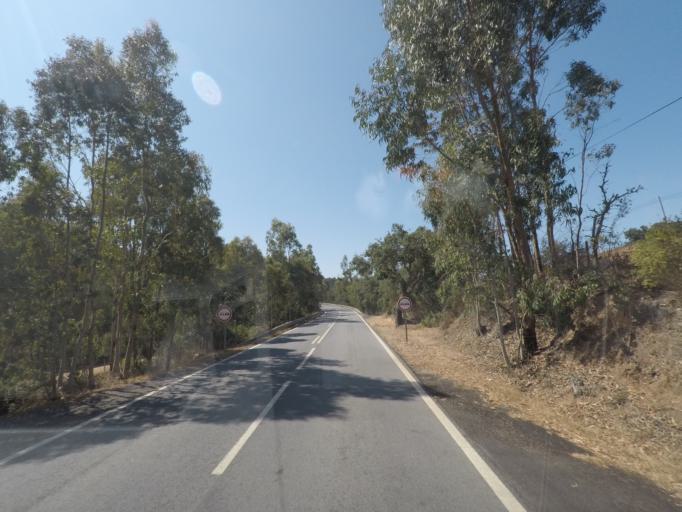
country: PT
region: Beja
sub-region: Odemira
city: Sao Teotonio
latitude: 37.5337
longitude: -8.6943
